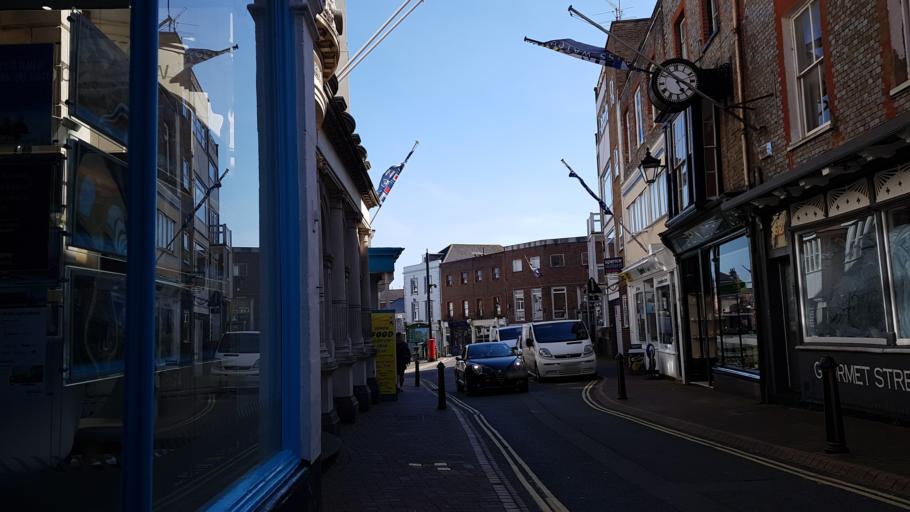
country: GB
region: England
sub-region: Isle of Wight
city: Cowes
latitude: 50.7645
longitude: -1.2987
